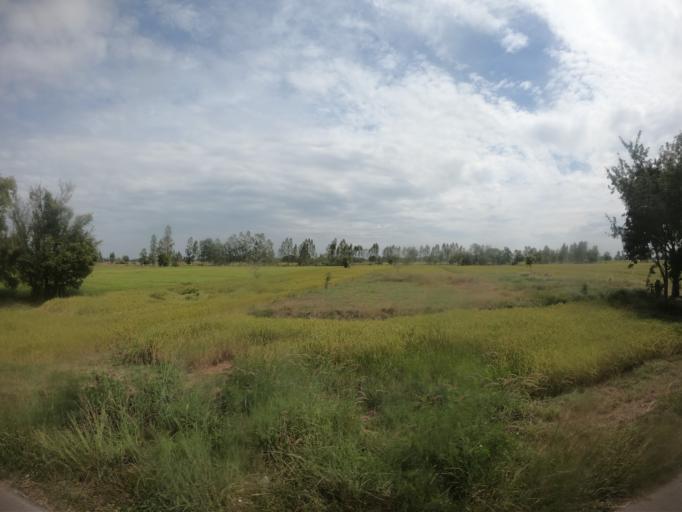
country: TH
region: Maha Sarakham
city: Chiang Yuen
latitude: 16.3782
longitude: 103.1040
